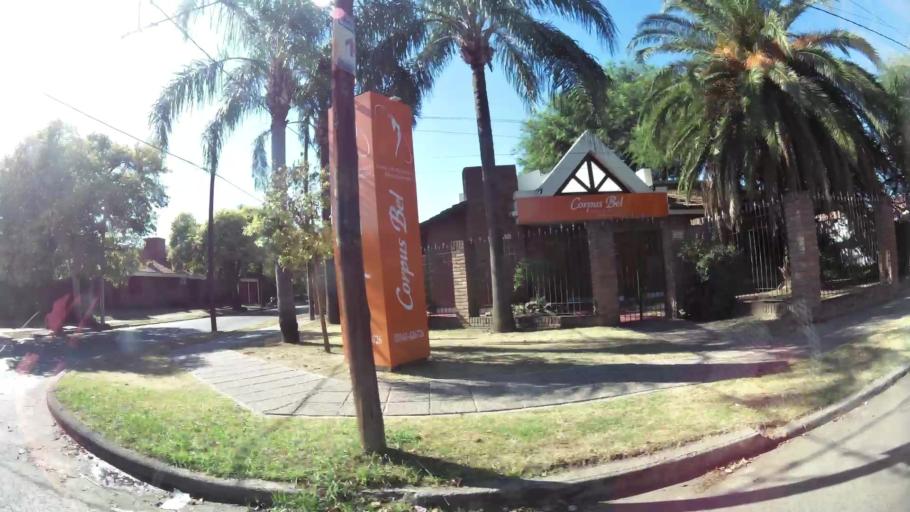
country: AR
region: Cordoba
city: Villa Allende
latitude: -31.3492
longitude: -64.2455
